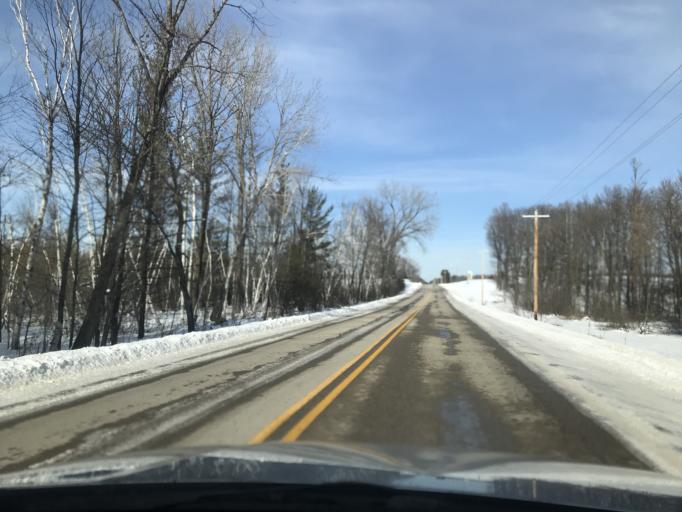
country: US
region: Wisconsin
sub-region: Oconto County
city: Oconto Falls
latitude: 45.1493
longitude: -88.1877
